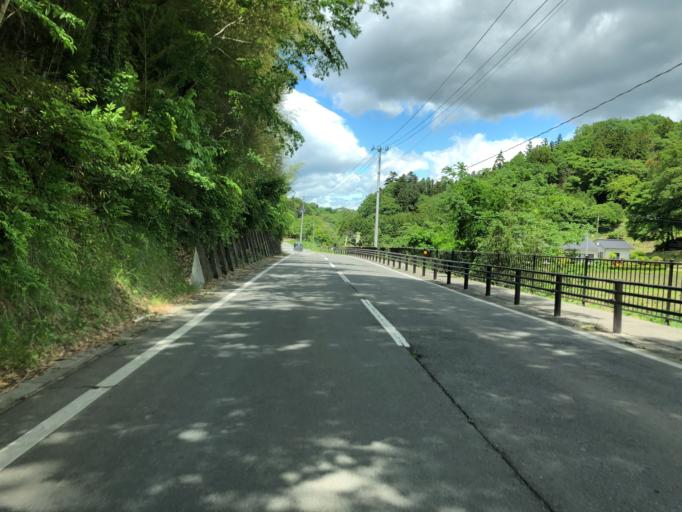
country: JP
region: Fukushima
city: Nihommatsu
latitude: 37.5383
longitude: 140.4734
